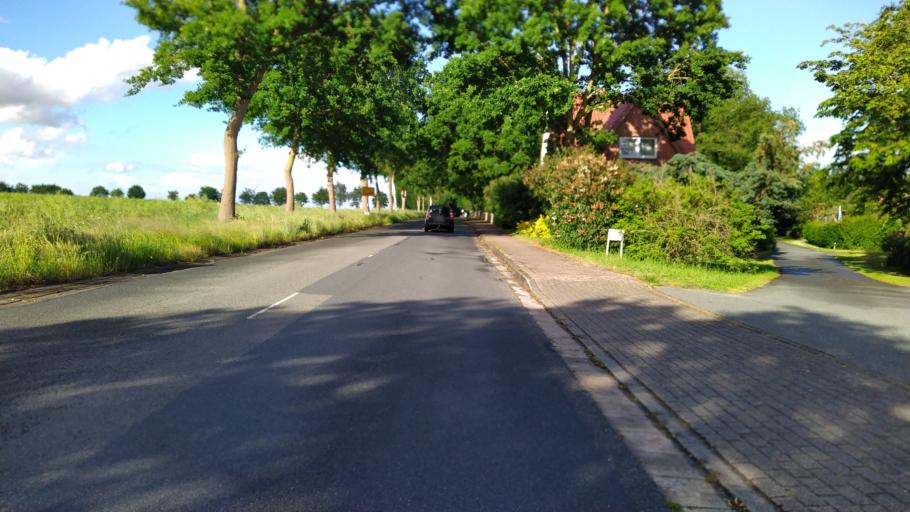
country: DE
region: Lower Saxony
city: Farven
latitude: 53.4455
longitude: 9.2777
